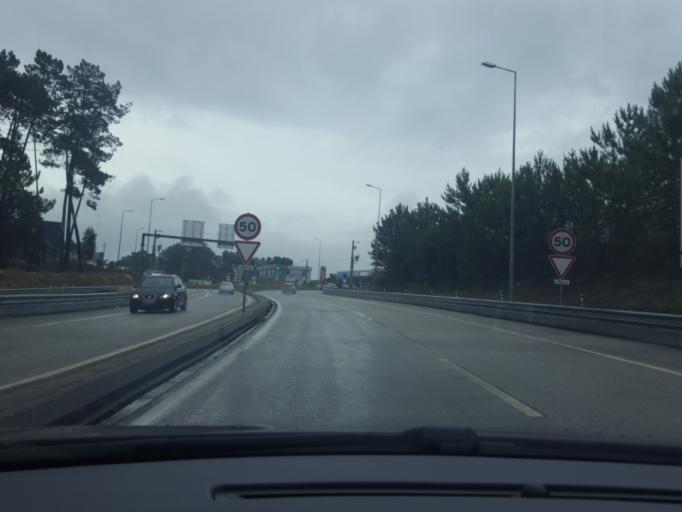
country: PT
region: Leiria
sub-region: Leiria
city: Leiria
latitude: 39.7363
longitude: -8.7699
